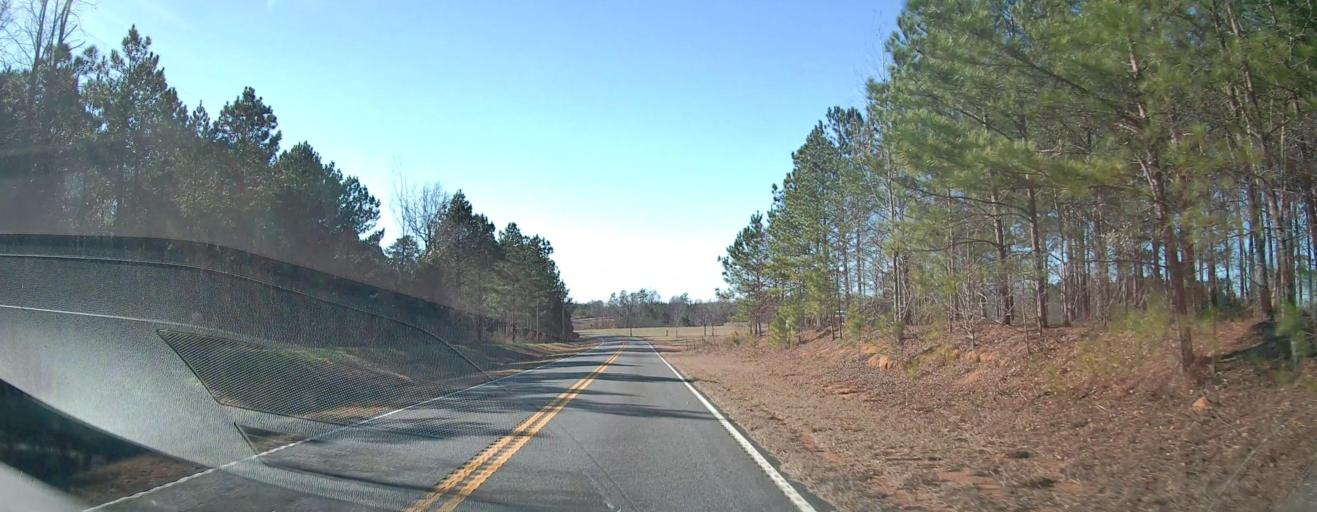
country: US
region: Georgia
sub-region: Talbot County
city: Talbotton
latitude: 32.6465
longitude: -84.3824
